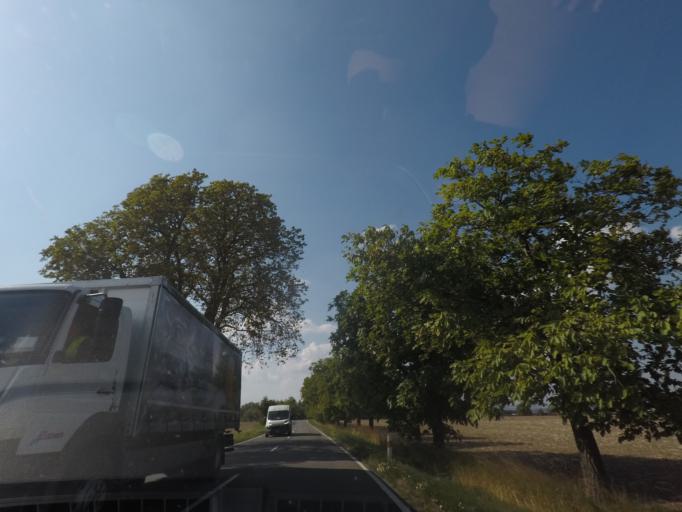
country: CZ
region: Kralovehradecky
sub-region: Okres Nachod
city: Jaromer
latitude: 50.3319
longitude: 15.9413
